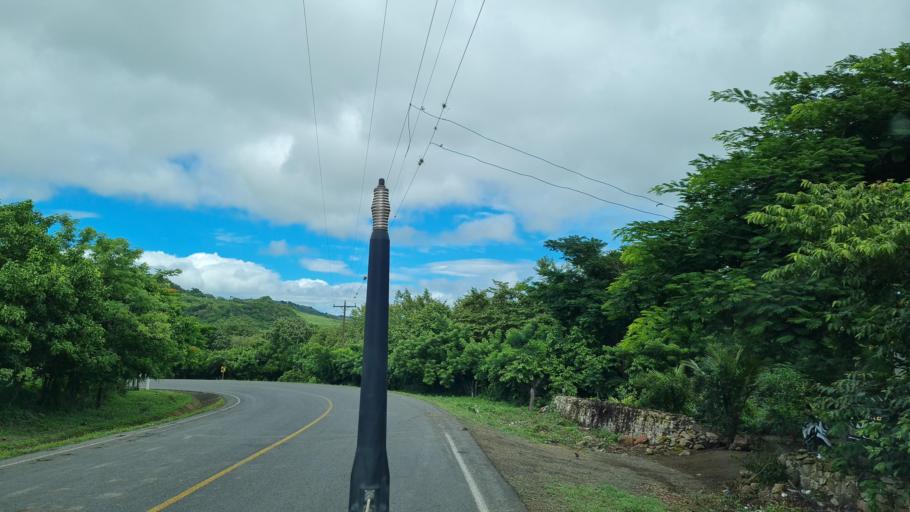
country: NI
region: Matagalpa
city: Terrabona
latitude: 12.5851
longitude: -85.9722
